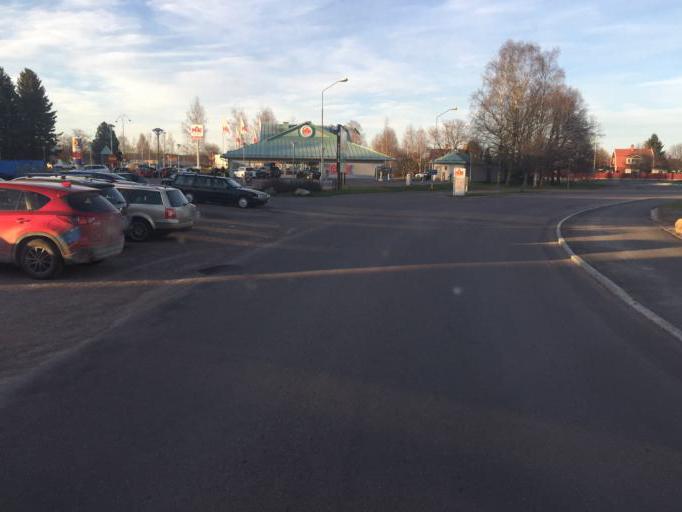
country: SE
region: Dalarna
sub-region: Borlange Kommun
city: Borlaenge
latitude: 60.4764
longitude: 15.4353
